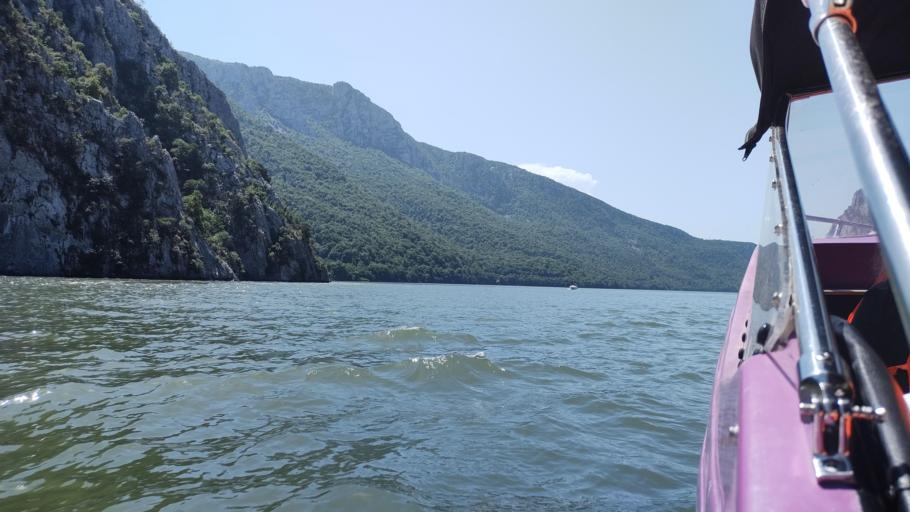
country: RO
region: Mehedinti
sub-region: Comuna Dubova
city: Dubova
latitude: 44.6134
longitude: 22.2721
